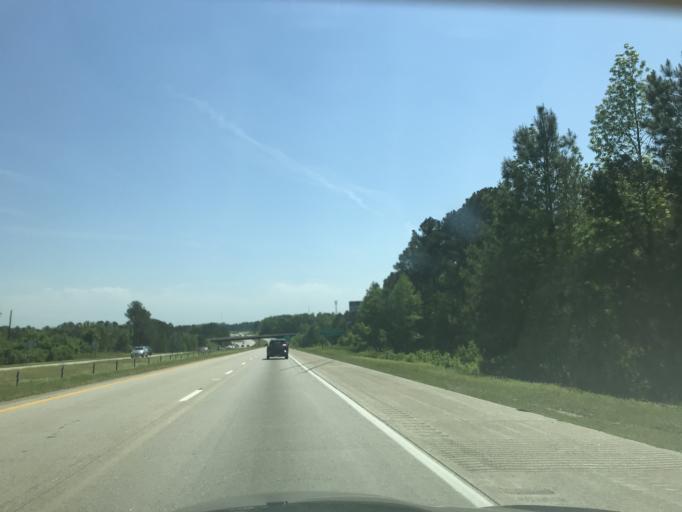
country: US
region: North Carolina
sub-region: Johnston County
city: Benson
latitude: 35.4023
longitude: -78.5234
